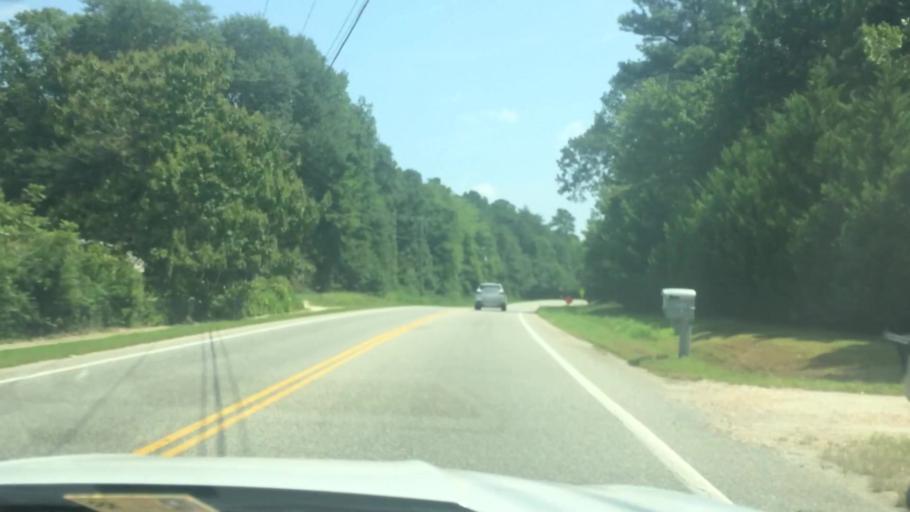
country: US
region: Virginia
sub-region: James City County
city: Williamsburg
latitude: 37.3388
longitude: -76.7623
